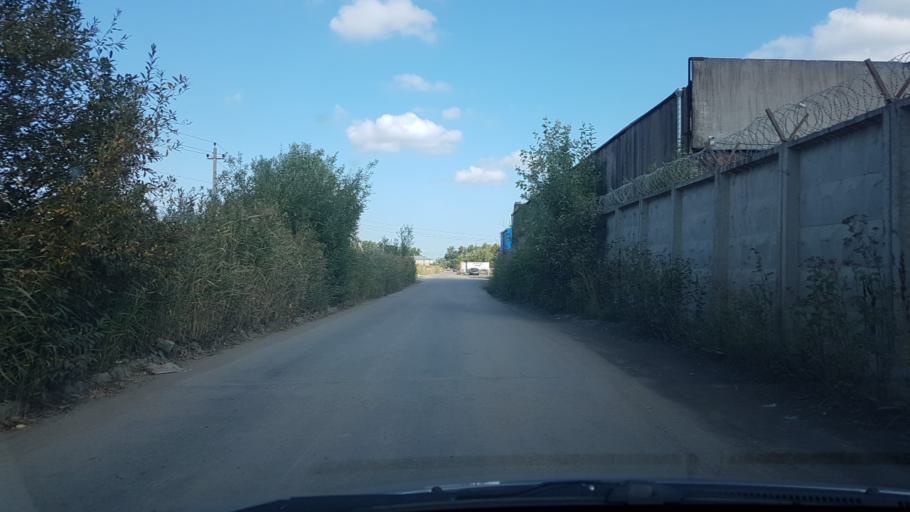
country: RU
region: St.-Petersburg
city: Sosnovaya Polyana
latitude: 59.8411
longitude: 30.1197
